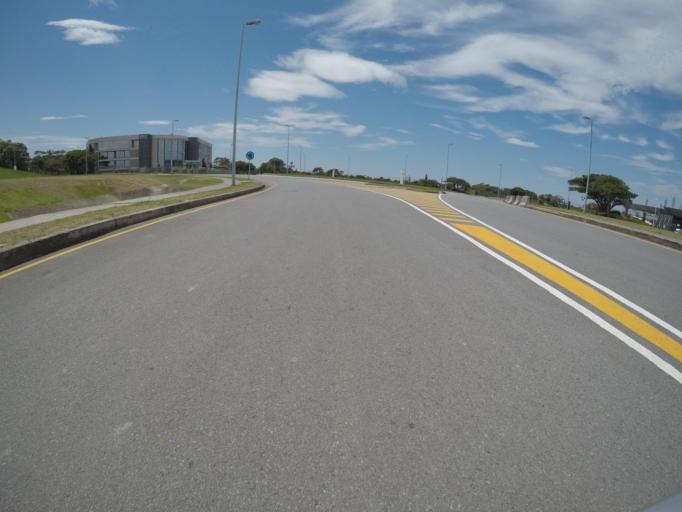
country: ZA
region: Eastern Cape
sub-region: Buffalo City Metropolitan Municipality
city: East London
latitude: -33.0494
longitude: 27.8525
